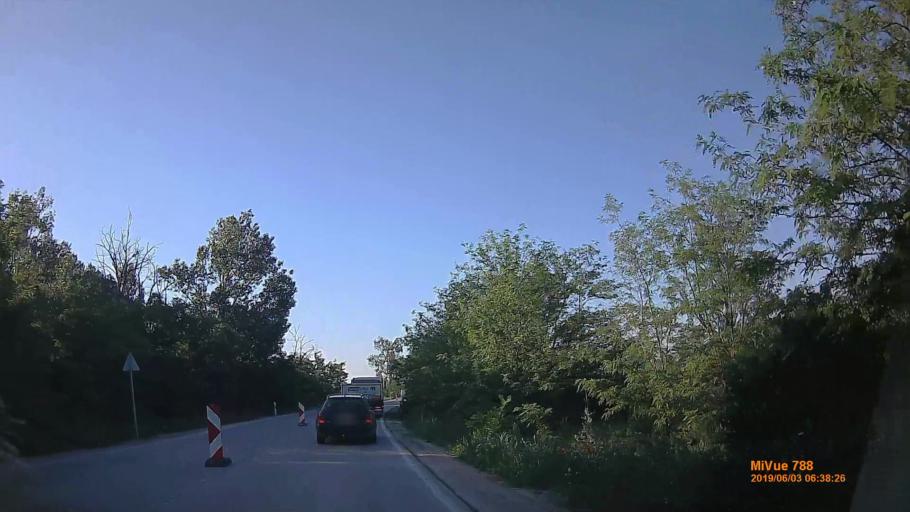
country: HU
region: Pest
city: Dunavarsany
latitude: 47.2949
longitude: 19.0938
